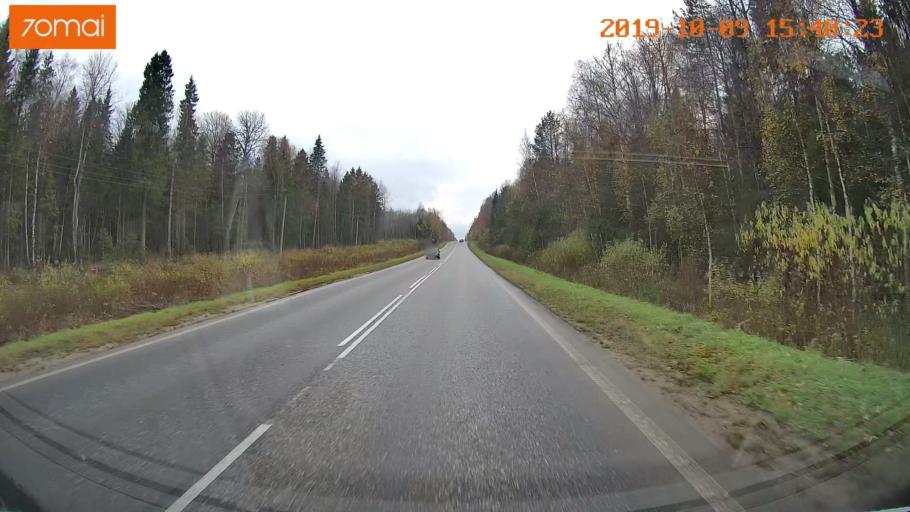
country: RU
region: Kostroma
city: Oktyabr'skiy
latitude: 57.8881
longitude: 41.1454
